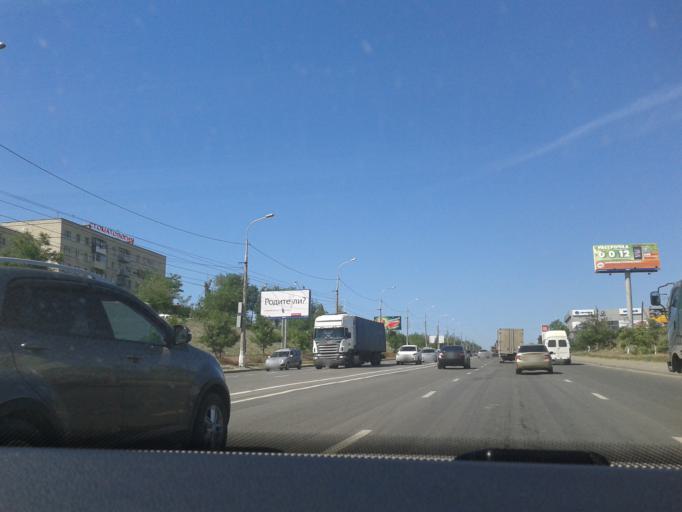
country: RU
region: Volgograd
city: Volgograd
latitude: 48.6672
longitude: 44.4412
